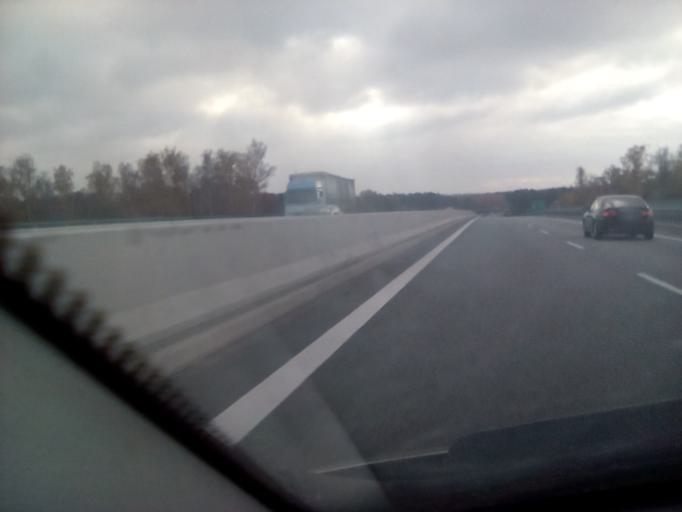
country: PL
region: Masovian Voivodeship
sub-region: Powiat bialobrzeski
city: Bialobrzegi
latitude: 51.6551
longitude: 20.9670
